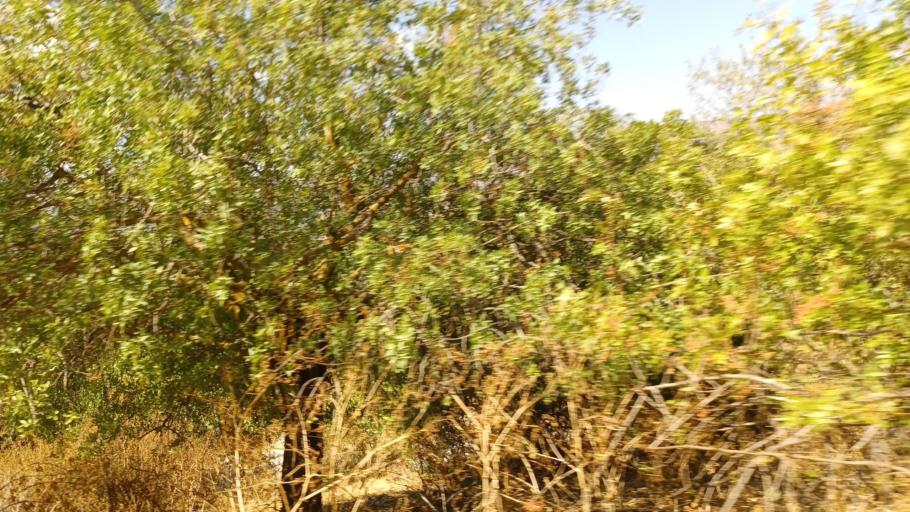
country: CY
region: Pafos
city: Polis
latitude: 34.9745
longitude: 32.4888
